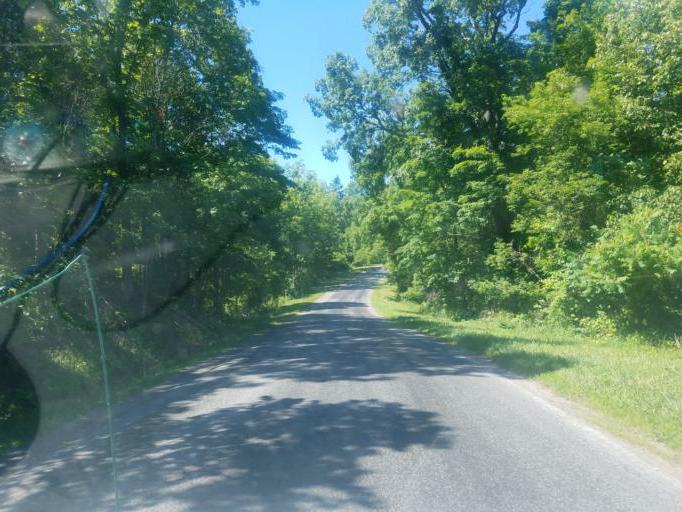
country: US
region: New York
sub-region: Ontario County
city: Naples
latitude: 42.7225
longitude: -77.3080
